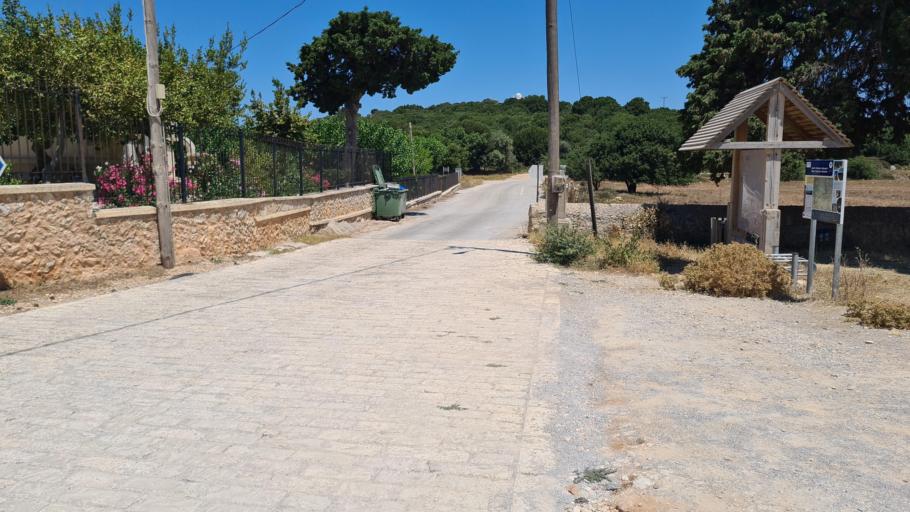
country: GR
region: Crete
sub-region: Nomos Rethymnis
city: Agia Foteini
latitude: 35.3106
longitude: 24.6284
